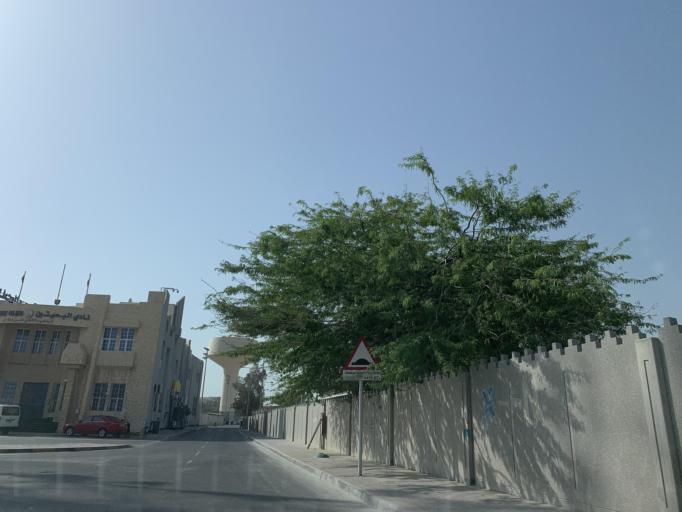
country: BH
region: Muharraq
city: Al Muharraq
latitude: 26.2683
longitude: 50.6134
